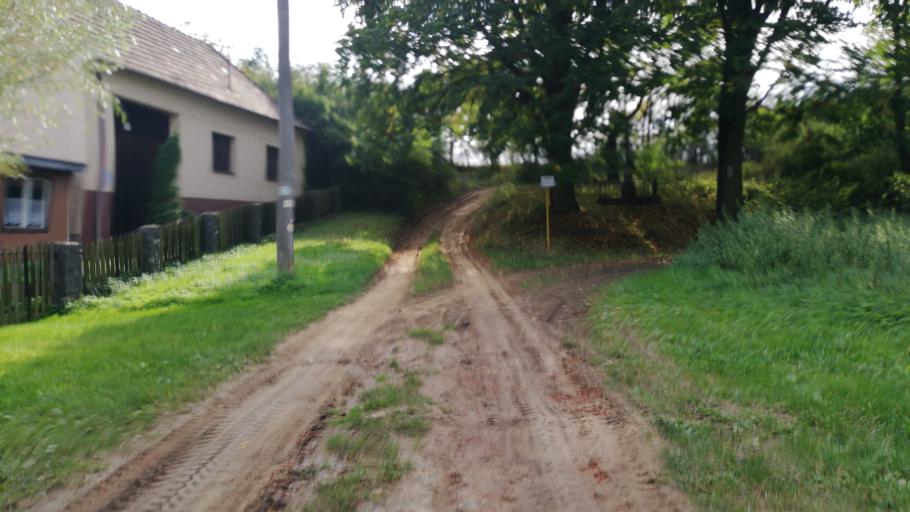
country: CZ
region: South Moravian
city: Sudomerice
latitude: 48.8189
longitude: 17.2822
